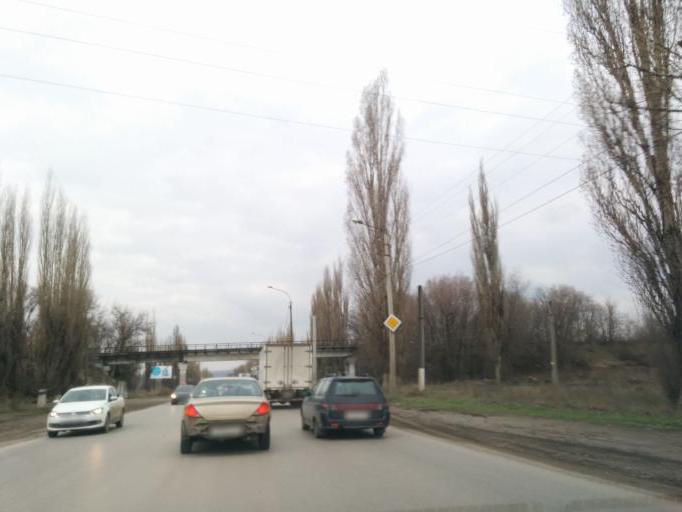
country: RU
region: Rostov
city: Novocherkassk
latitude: 47.4791
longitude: 40.1027
